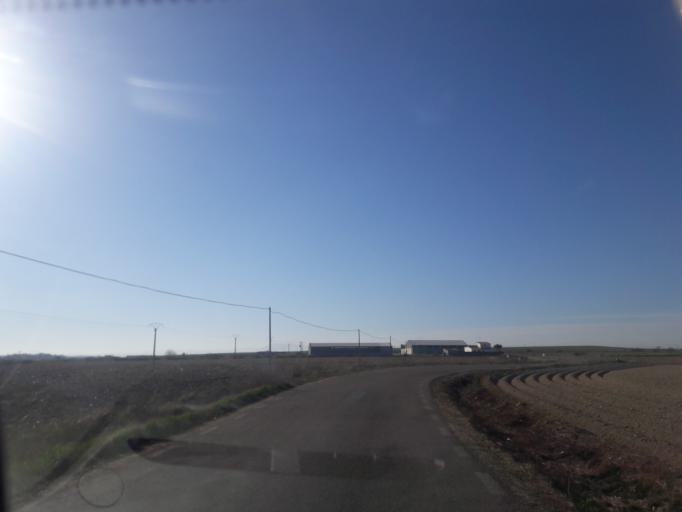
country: ES
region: Castille and Leon
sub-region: Provincia de Salamanca
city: Penarandilla
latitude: 40.8792
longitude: -5.3910
